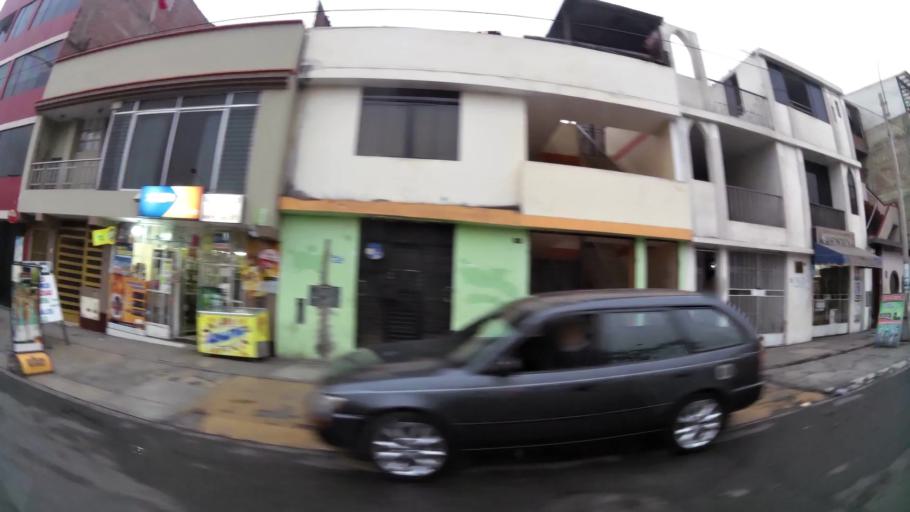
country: PE
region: Lima
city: Lima
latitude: -12.0120
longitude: -76.9842
